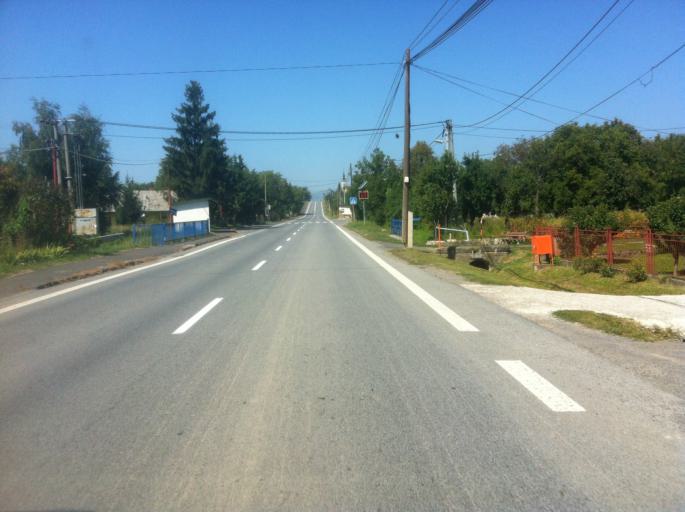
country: SK
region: Kosicky
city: Sobrance
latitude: 48.7054
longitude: 22.2257
